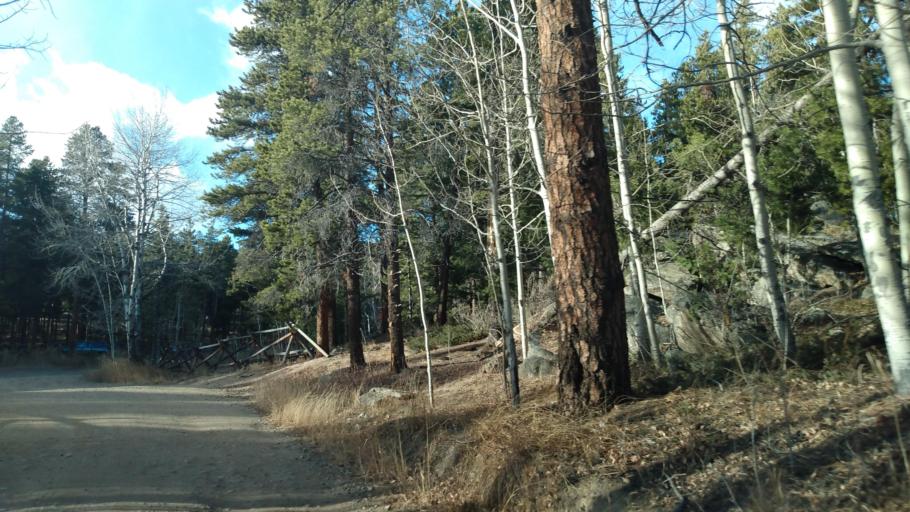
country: US
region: Colorado
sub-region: Boulder County
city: Nederland
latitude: 39.9569
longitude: -105.4465
